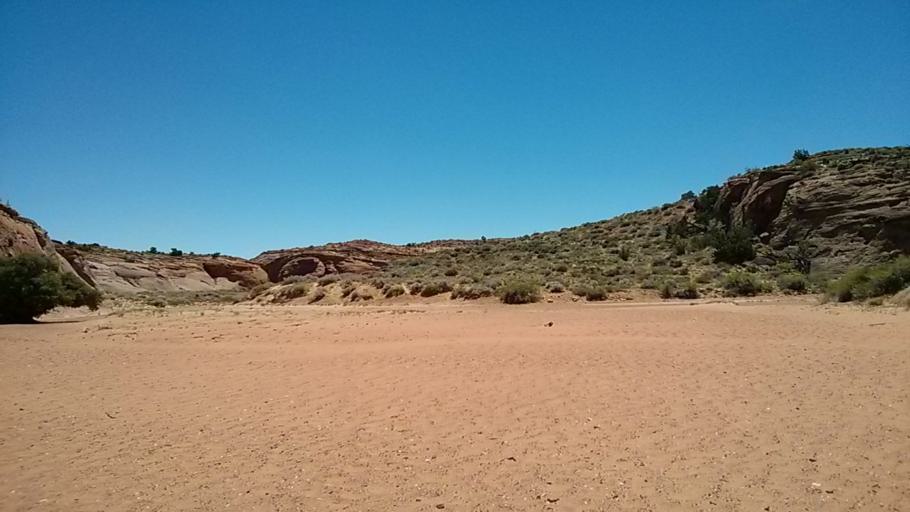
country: US
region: Arizona
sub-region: Coconino County
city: Page
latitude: 37.4805
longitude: -111.2091
